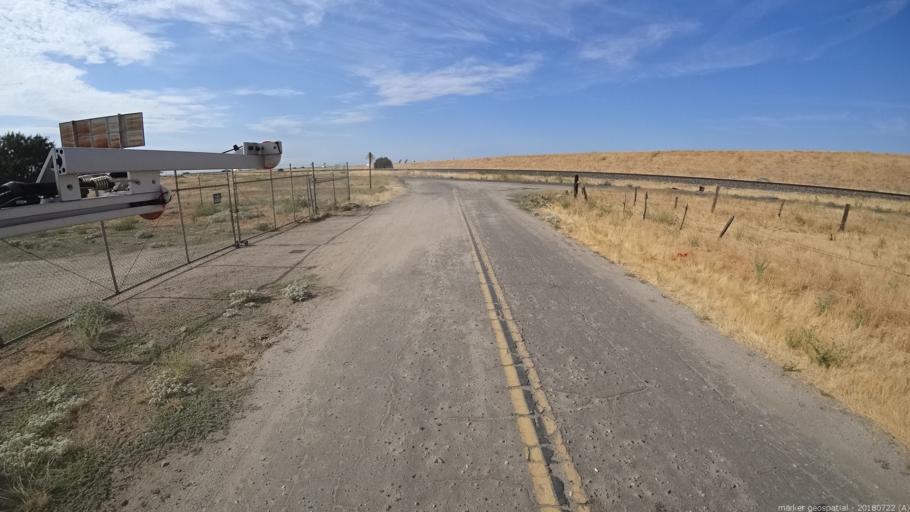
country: US
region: California
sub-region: Madera County
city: Fairmead
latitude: 37.0657
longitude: -120.1841
